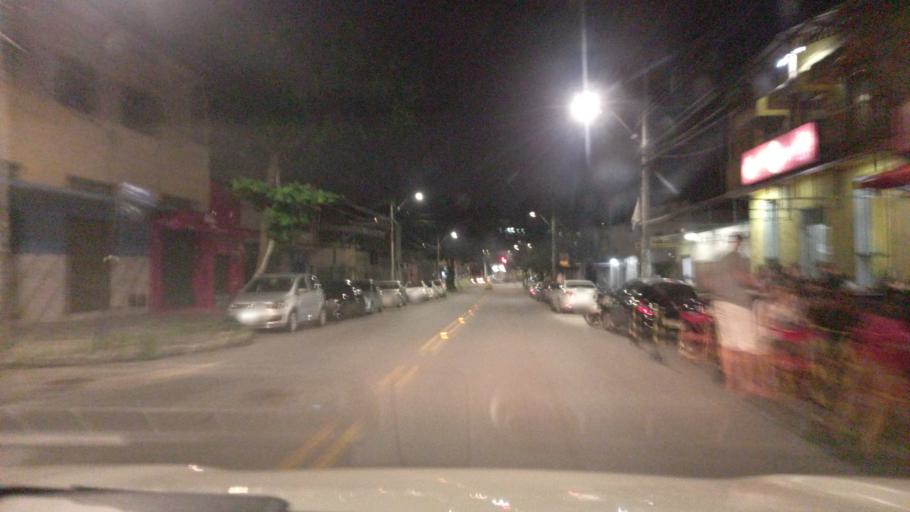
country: BR
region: Minas Gerais
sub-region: Belo Horizonte
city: Belo Horizonte
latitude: -19.8847
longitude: -43.9400
